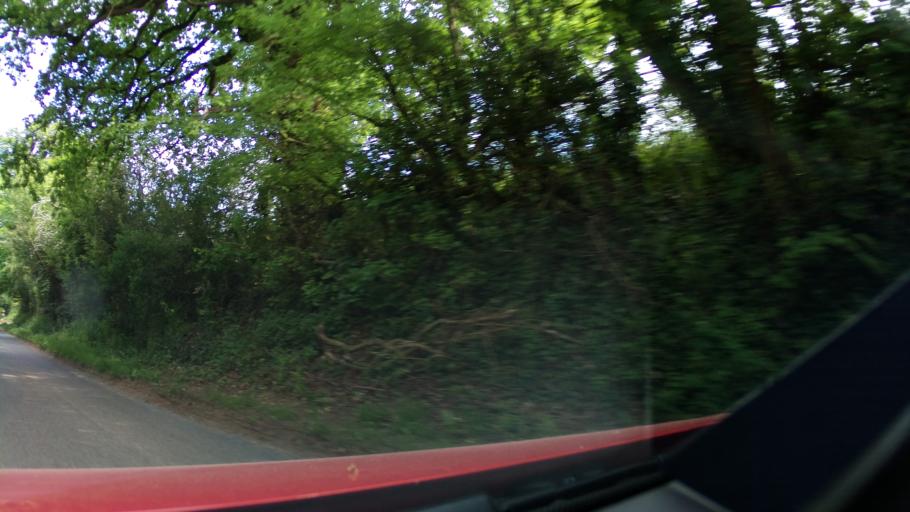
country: GB
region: England
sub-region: Gloucestershire
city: Chipping Campden
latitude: 52.0496
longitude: -1.7921
